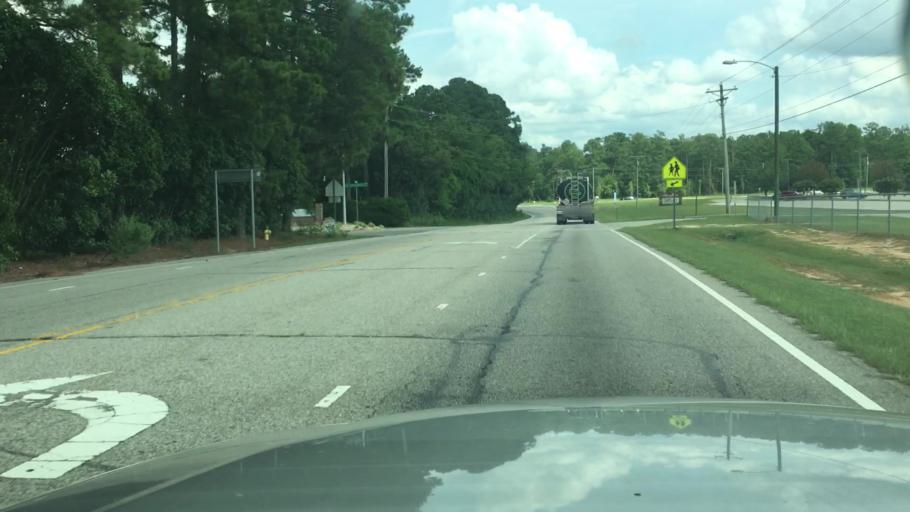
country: US
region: North Carolina
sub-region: Cumberland County
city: Hope Mills
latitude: 35.0019
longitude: -78.9900
